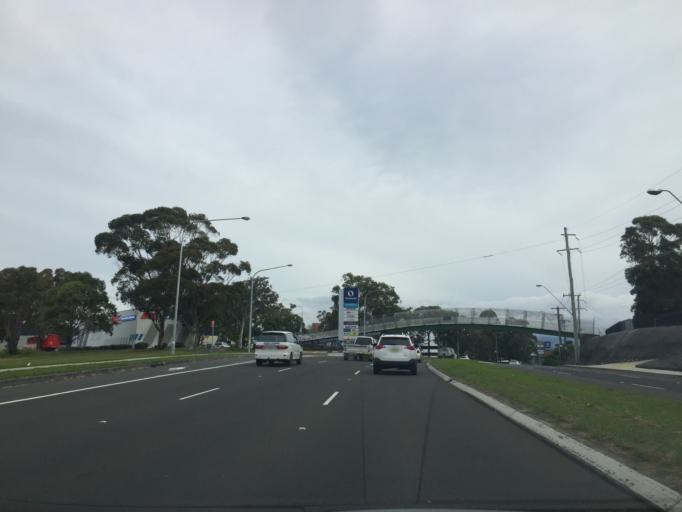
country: AU
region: New South Wales
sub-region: Shellharbour
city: Barrack Heights
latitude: -34.5612
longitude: 150.8414
